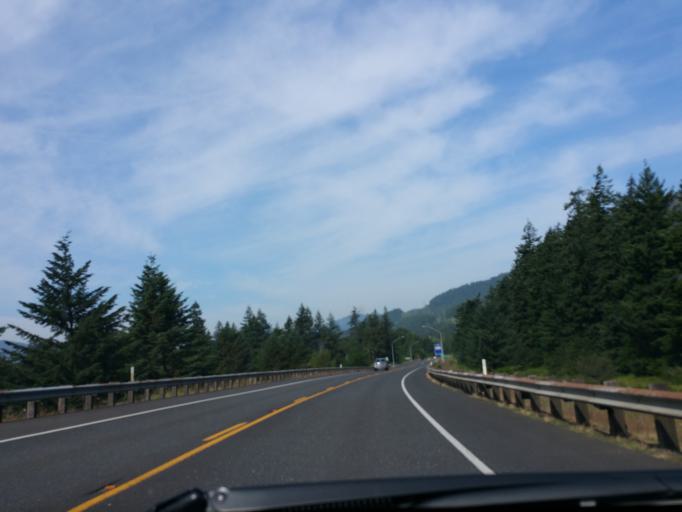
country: US
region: Oregon
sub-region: Hood River County
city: Cascade Locks
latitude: 45.6412
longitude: -121.9704
